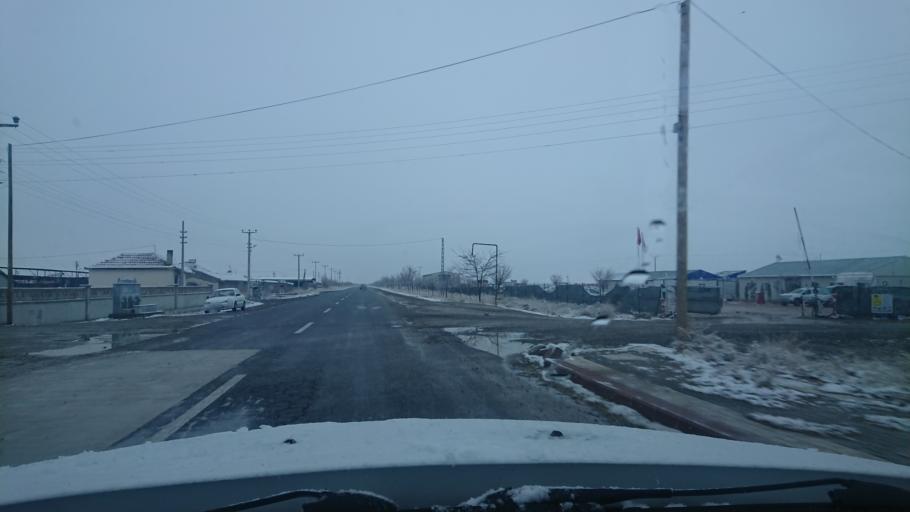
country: TR
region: Aksaray
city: Yesilova
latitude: 38.2967
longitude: 33.7584
